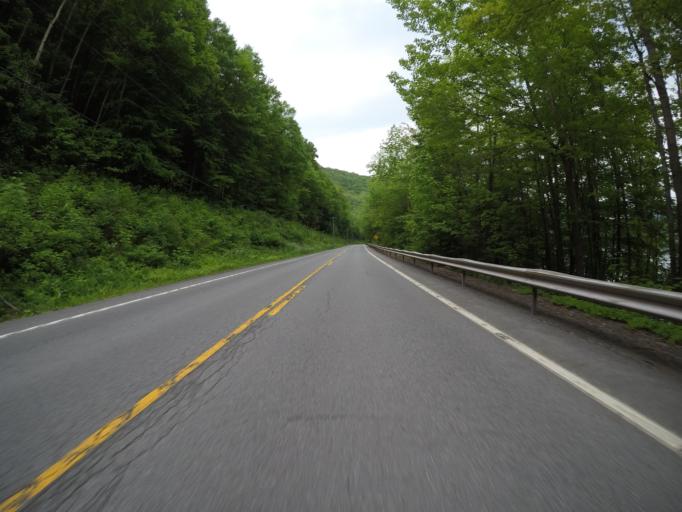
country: US
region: New York
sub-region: Sullivan County
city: Livingston Manor
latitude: 42.0733
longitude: -74.9197
